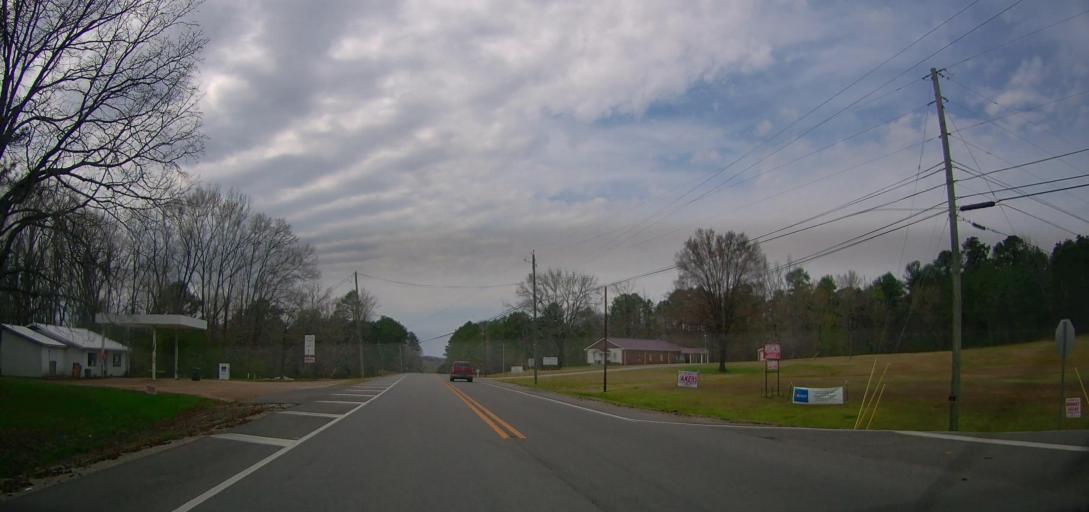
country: US
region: Alabama
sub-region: Marion County
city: Guin
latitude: 33.9862
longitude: -87.9205
